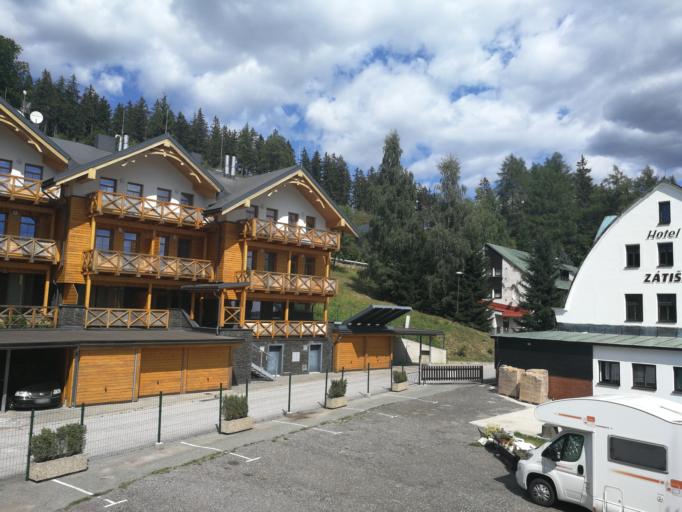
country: CZ
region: Kralovehradecky
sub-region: Okres Trutnov
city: Svoboda nad Upou
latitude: 50.6323
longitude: 15.7698
